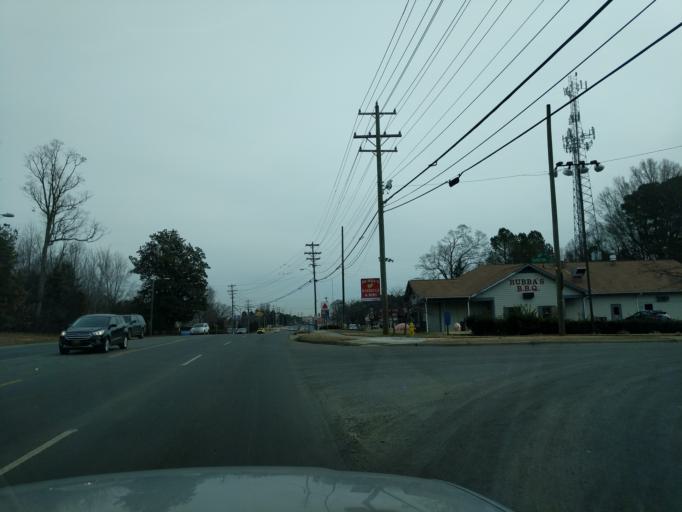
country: US
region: North Carolina
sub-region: Mecklenburg County
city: Charlotte
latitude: 35.3061
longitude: -80.8548
